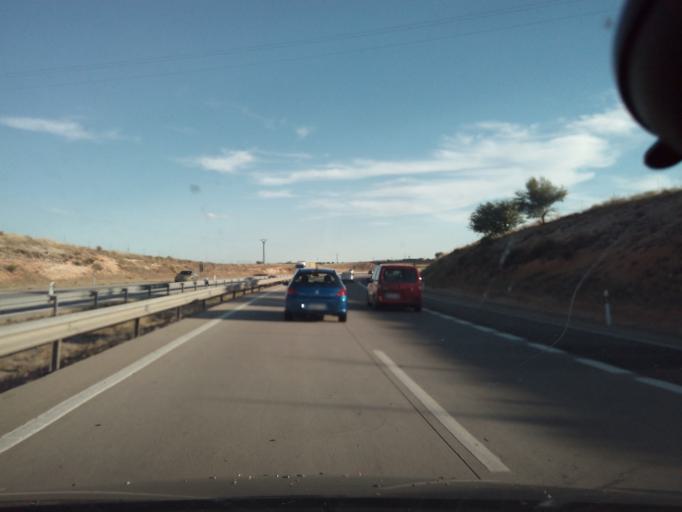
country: ES
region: Castille-La Mancha
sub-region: Province of Toledo
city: Dosbarrios
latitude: 39.8860
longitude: -3.4708
